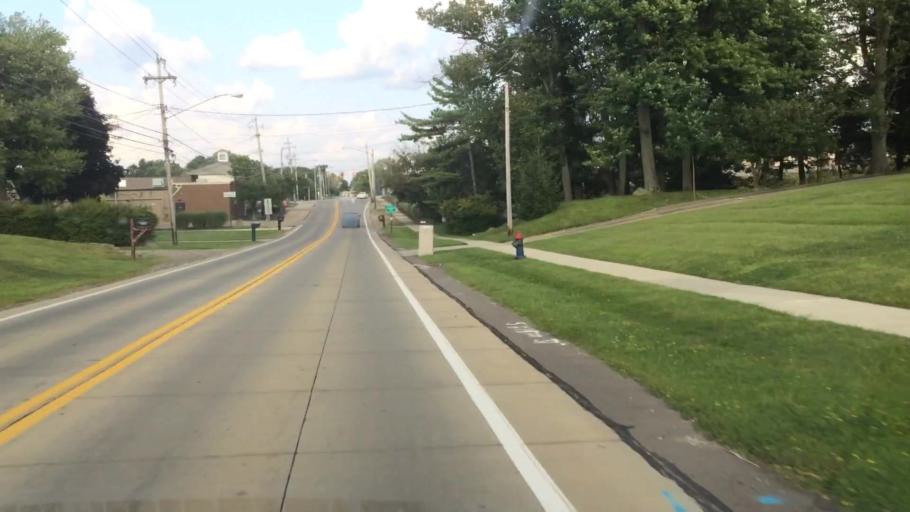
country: US
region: Ohio
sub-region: Cuyahoga County
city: Broadview Heights
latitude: 41.3509
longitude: -81.6888
